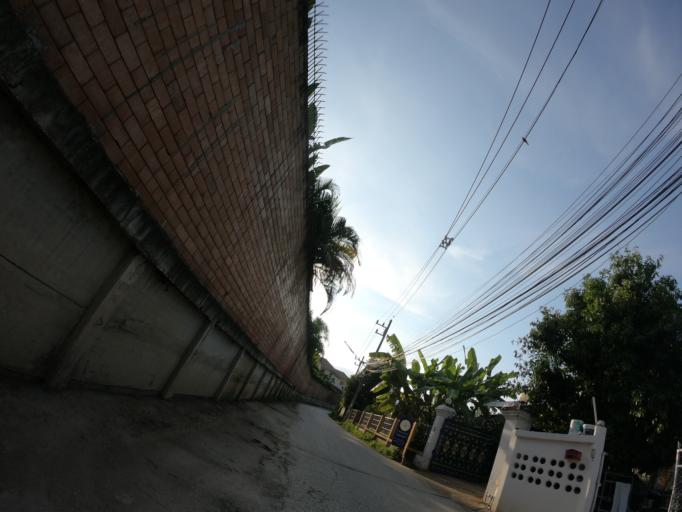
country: TH
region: Chiang Mai
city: Chiang Mai
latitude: 18.8338
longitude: 98.9798
